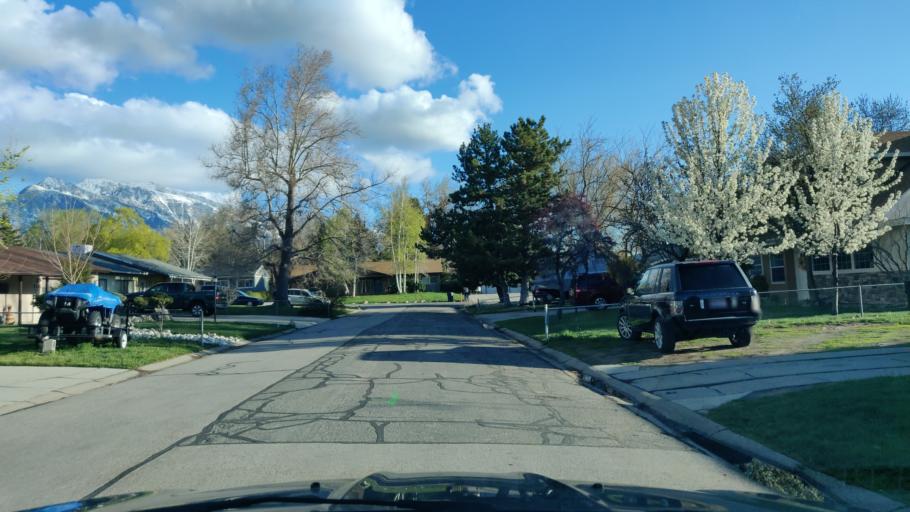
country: US
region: Utah
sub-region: Salt Lake County
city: Cottonwood Heights
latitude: 40.6188
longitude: -111.8099
